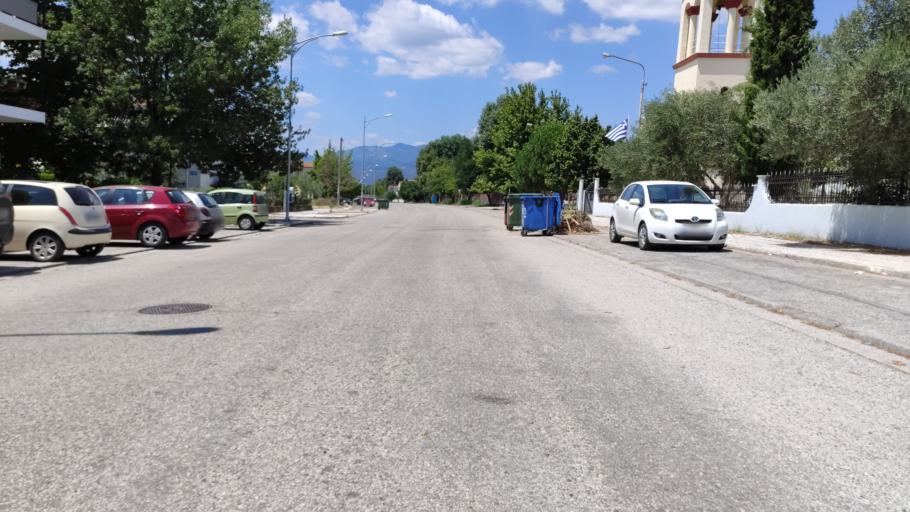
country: GR
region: East Macedonia and Thrace
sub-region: Nomos Rodopis
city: Komotini
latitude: 41.1257
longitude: 25.3983
